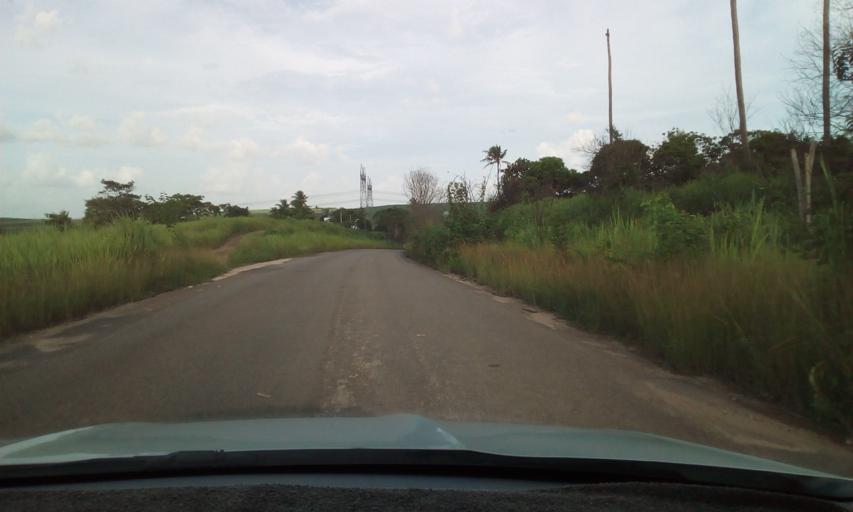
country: BR
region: Pernambuco
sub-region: Gloria Do Goita
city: Gloria do Goita
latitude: -7.9883
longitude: -35.2391
